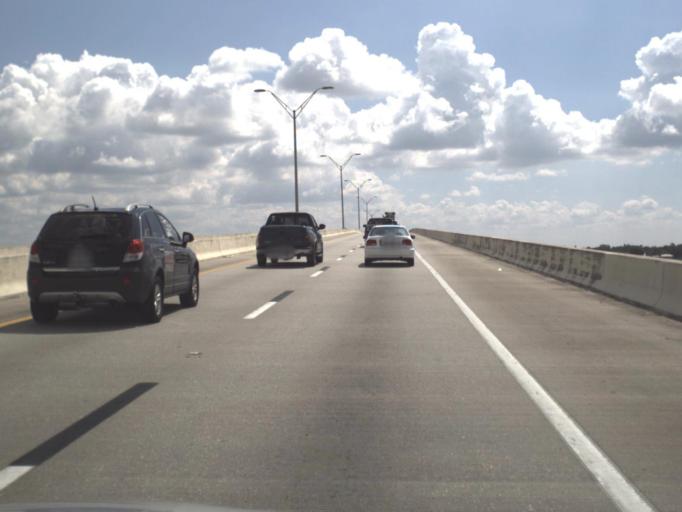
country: US
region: Florida
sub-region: Lee County
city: Whiskey Creek
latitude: 26.6026
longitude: -81.9032
